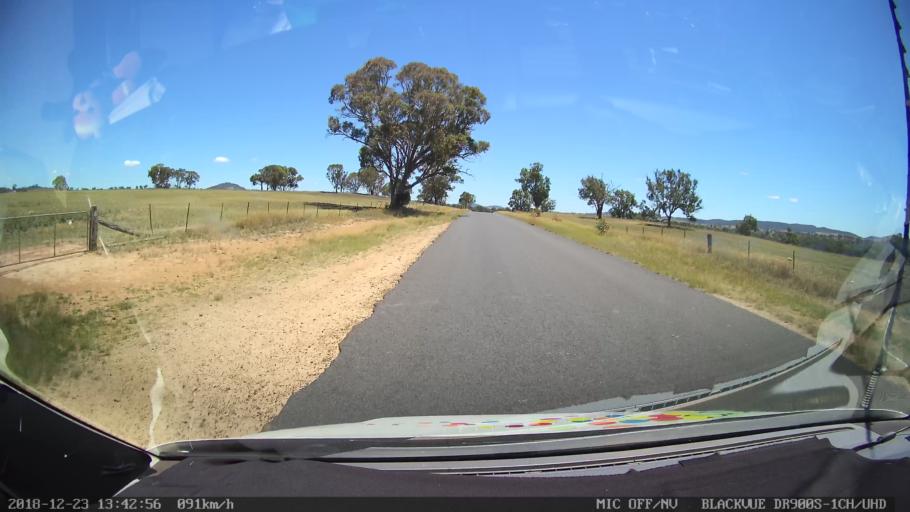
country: AU
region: New South Wales
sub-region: Tamworth Municipality
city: Manilla
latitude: -30.4820
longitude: 151.1569
